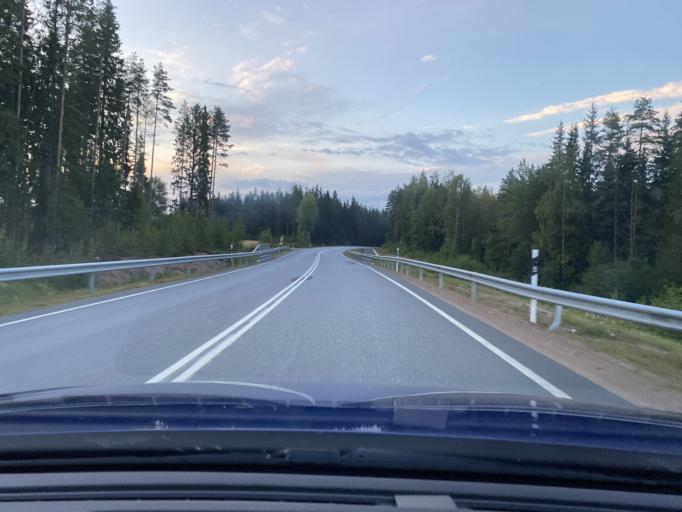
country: FI
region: Satakunta
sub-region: Pohjois-Satakunta
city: Honkajoki
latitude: 62.0220
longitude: 22.2289
